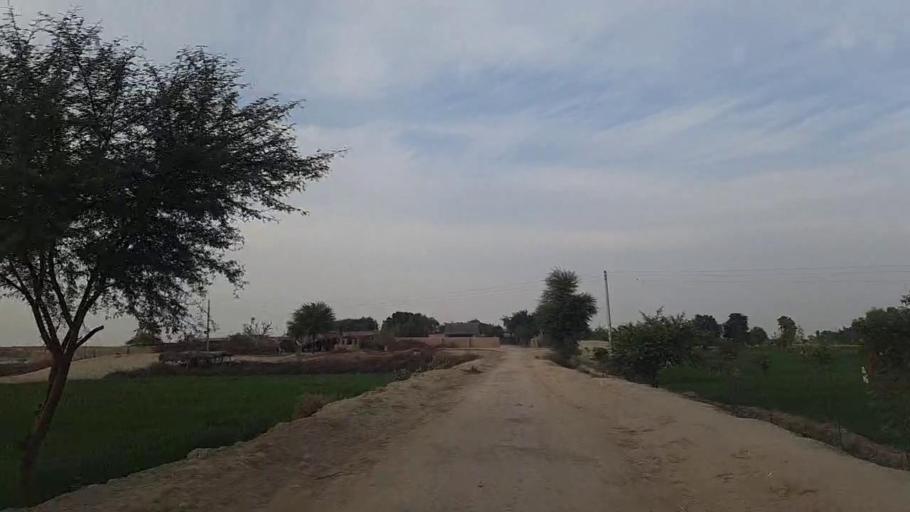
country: PK
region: Sindh
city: Jam Sahib
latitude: 26.4653
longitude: 68.5622
